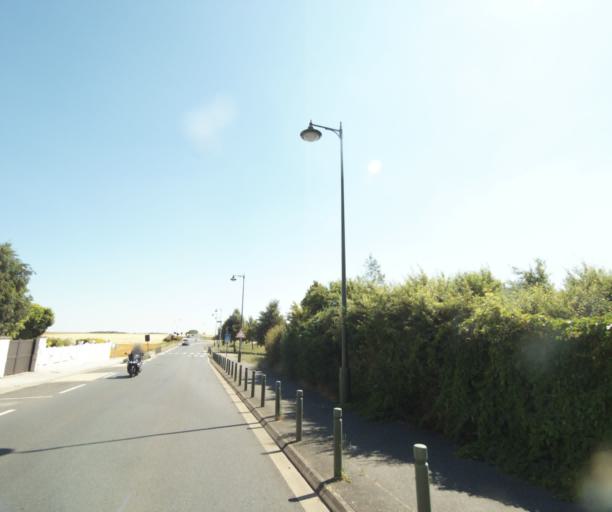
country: FR
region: Ile-de-France
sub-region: Departement de Seine-et-Marne
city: La Chapelle-la-Reine
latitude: 48.3102
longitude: 2.5727
